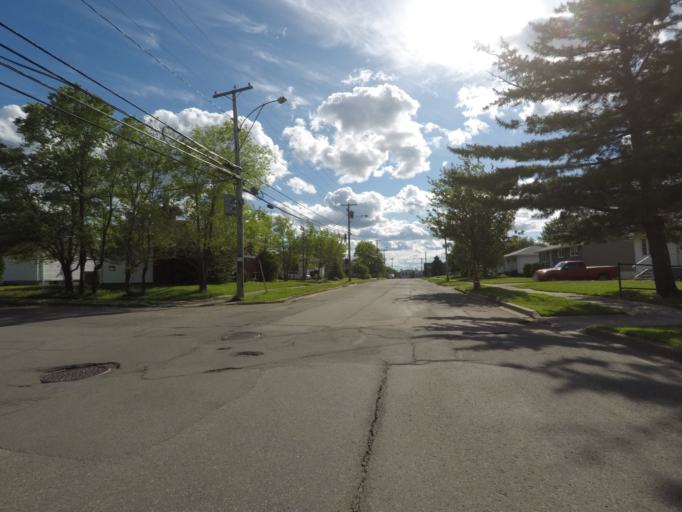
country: CA
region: New Brunswick
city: Moncton
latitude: 46.1034
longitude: -64.8276
